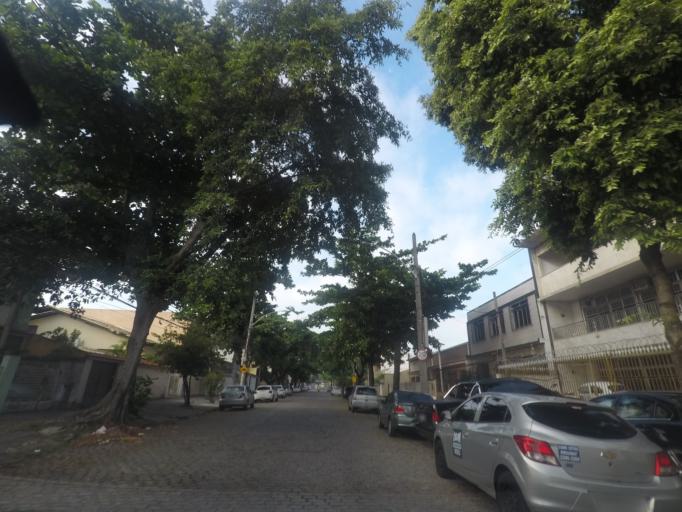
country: BR
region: Rio de Janeiro
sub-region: Duque De Caxias
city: Duque de Caxias
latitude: -22.8383
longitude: -43.2651
